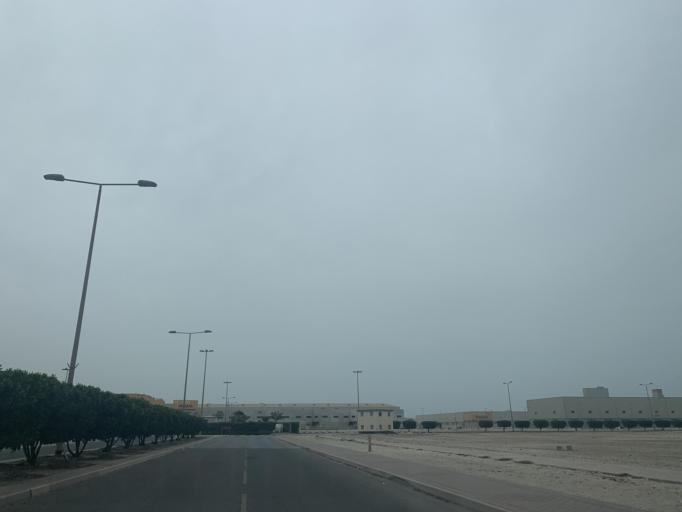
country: BH
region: Muharraq
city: Al Hadd
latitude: 26.2119
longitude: 50.6728
